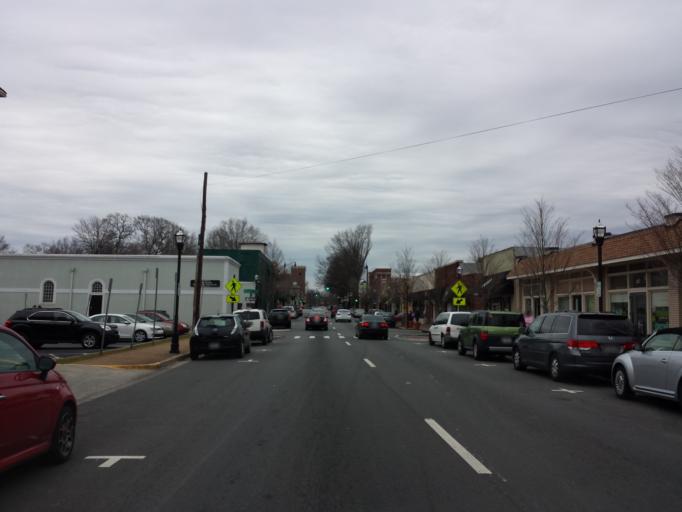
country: US
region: Georgia
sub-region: Cobb County
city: Marietta
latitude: 33.9544
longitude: -84.5502
